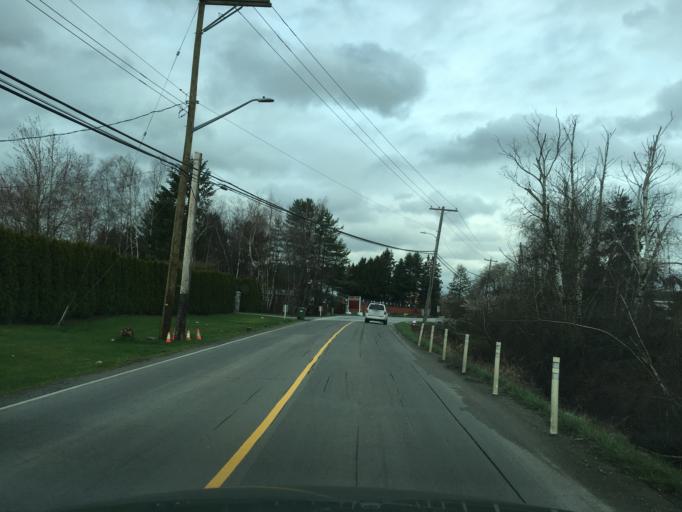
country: CA
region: British Columbia
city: Richmond
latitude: 49.1619
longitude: -123.0689
